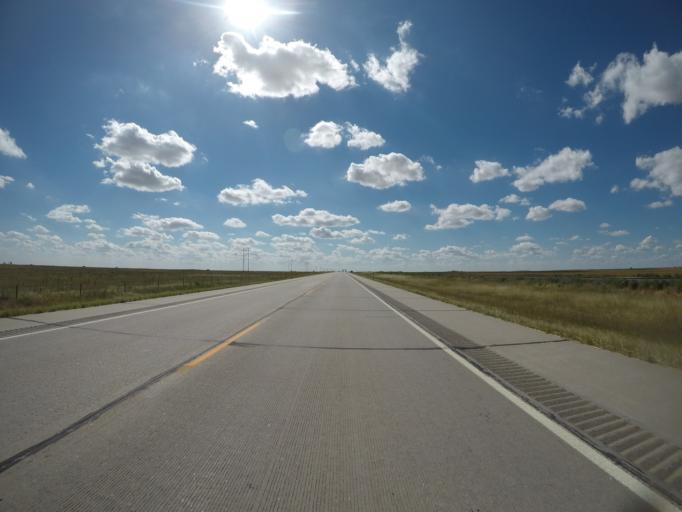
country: US
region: Colorado
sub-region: Phillips County
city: Holyoke
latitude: 40.6025
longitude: -102.4119
